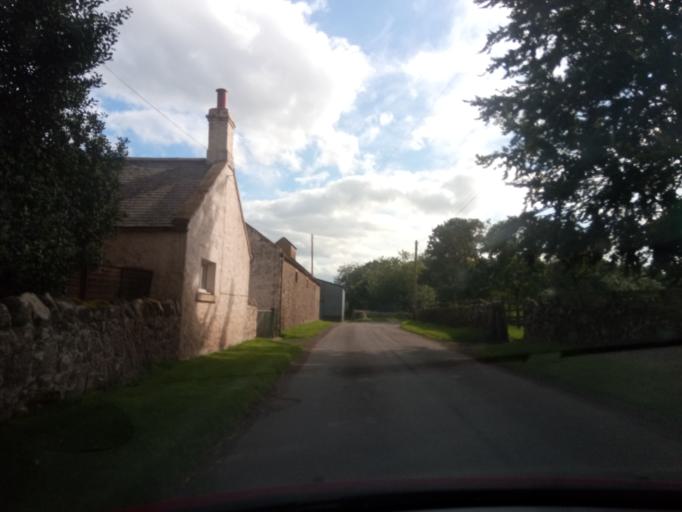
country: GB
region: Scotland
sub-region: The Scottish Borders
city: Coldstream
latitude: 55.5890
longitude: -2.2533
